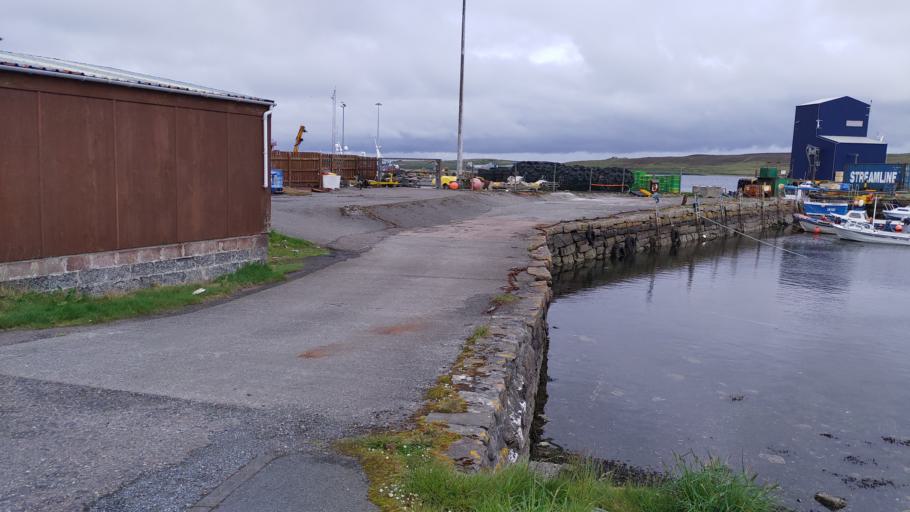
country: GB
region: Scotland
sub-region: Shetland Islands
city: Lerwick
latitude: 60.1588
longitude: -1.1556
